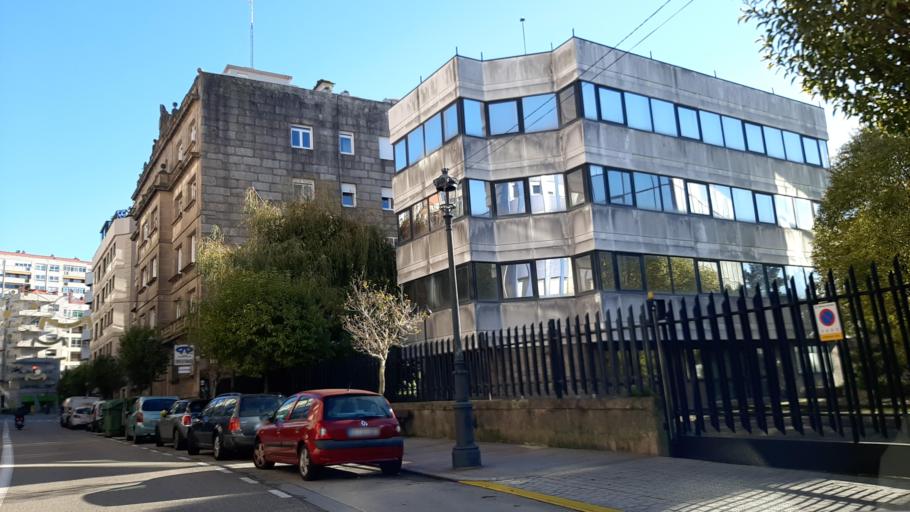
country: ES
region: Galicia
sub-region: Provincia de Pontevedra
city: Vigo
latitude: 42.2268
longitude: -8.7322
